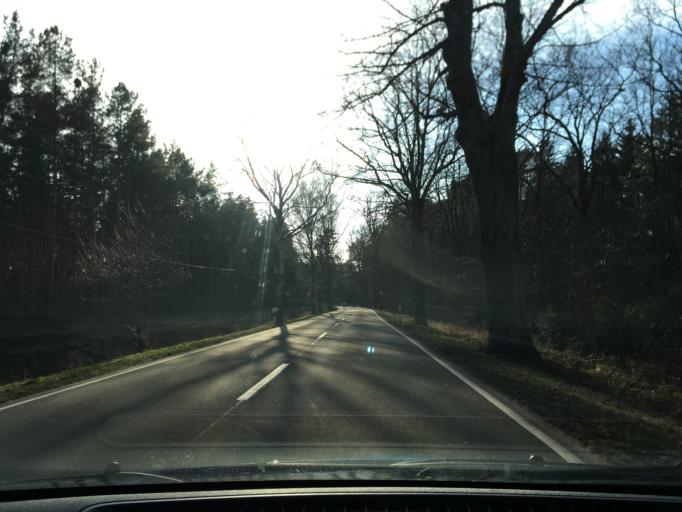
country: DE
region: Saxony-Anhalt
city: Seehausen
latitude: 52.8867
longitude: 11.6574
